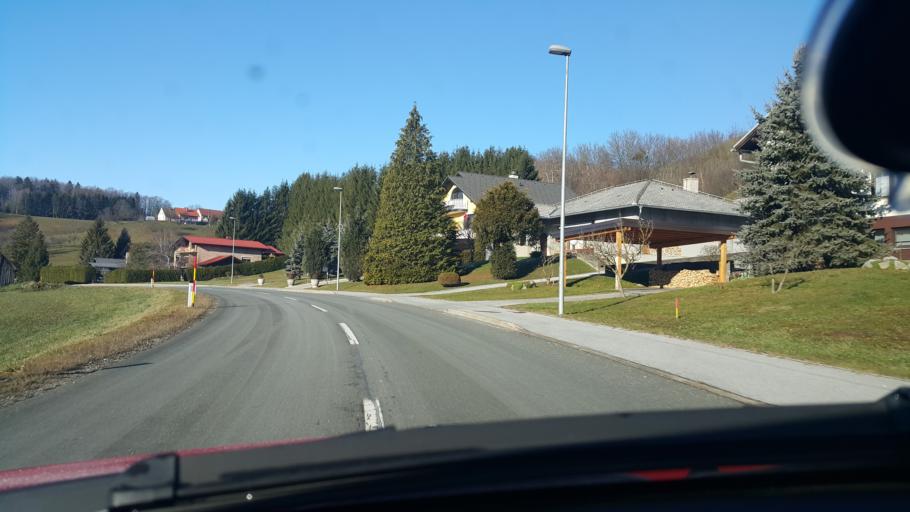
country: AT
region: Styria
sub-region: Politischer Bezirk Leibnitz
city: Sulztal an der Weinstrasse
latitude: 46.6469
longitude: 15.5647
